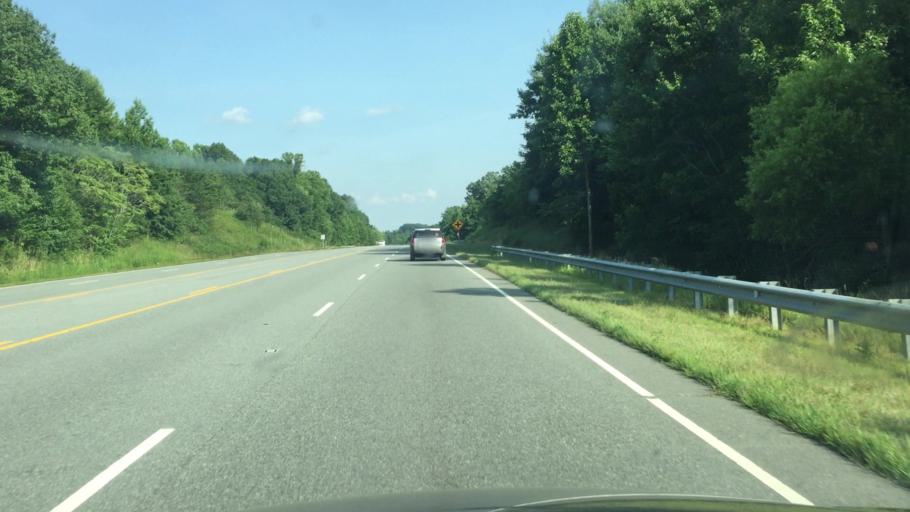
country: US
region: North Carolina
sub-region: Rockingham County
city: Reidsville
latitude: 36.3704
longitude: -79.6463
